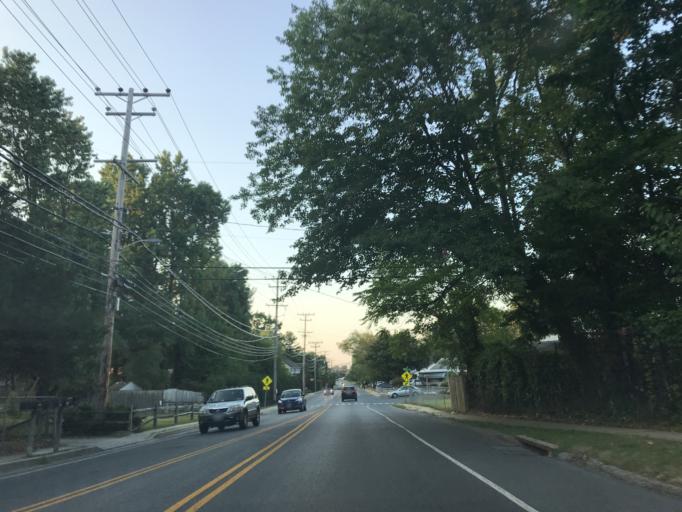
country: US
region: Maryland
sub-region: Anne Arundel County
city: Hillsmere Shores
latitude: 38.9532
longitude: -76.4936
